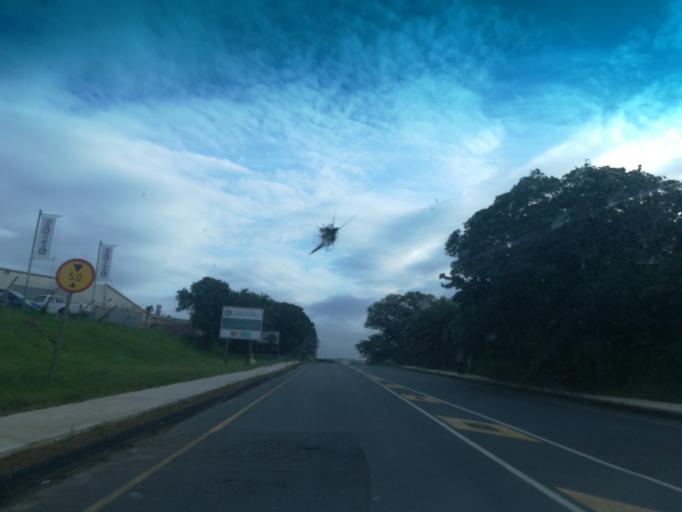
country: ZA
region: KwaZulu-Natal
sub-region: Ugu District Municipality
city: Scottburgh
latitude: -30.2935
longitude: 30.7413
